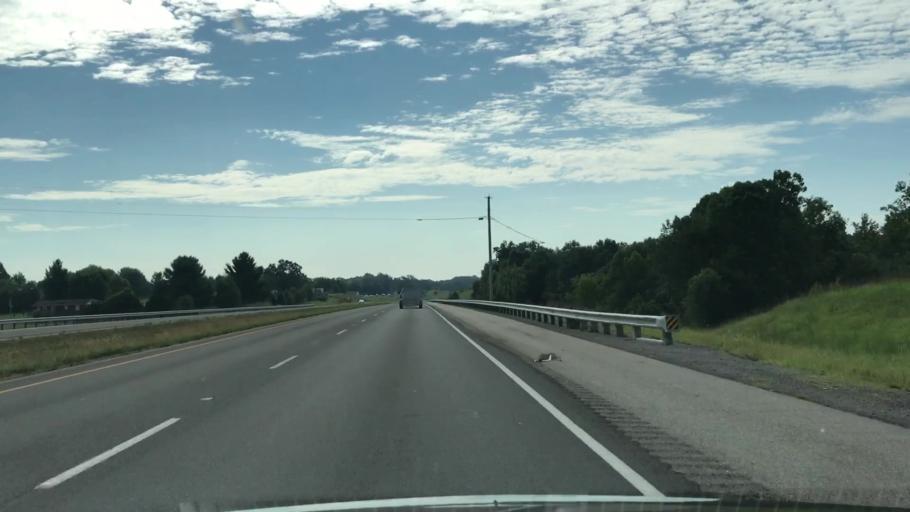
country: US
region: Kentucky
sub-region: Warren County
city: Plano
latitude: 36.8386
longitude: -86.3214
